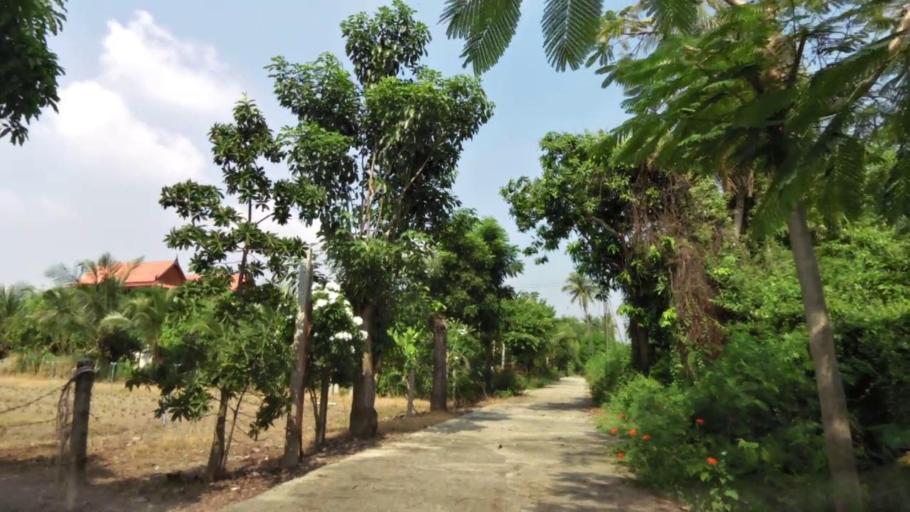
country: TH
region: Ang Thong
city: Wiset Chaichan
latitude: 14.6079
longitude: 100.3950
